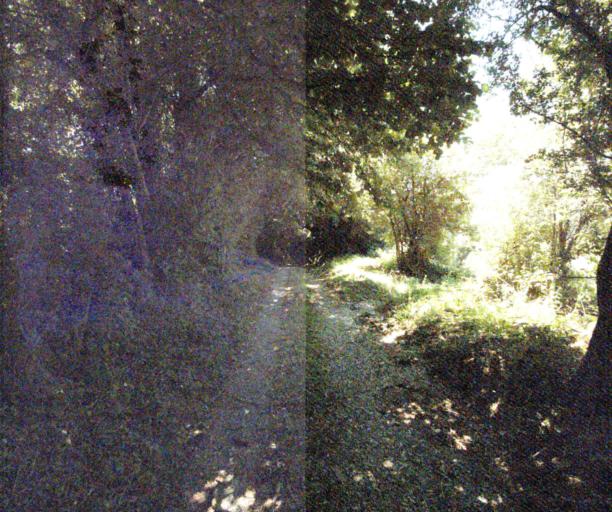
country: FR
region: Midi-Pyrenees
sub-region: Departement du Tarn
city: Dourgne
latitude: 43.4250
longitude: 2.1648
